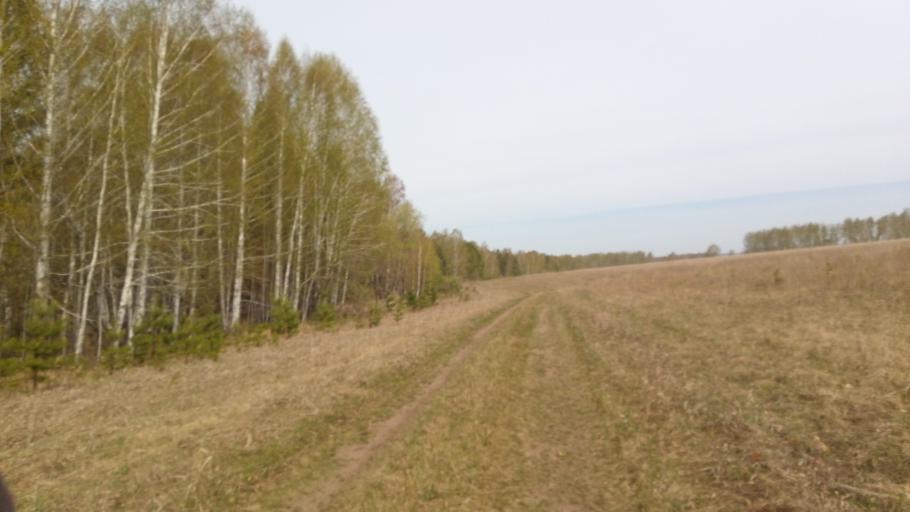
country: RU
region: Chelyabinsk
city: Timiryazevskiy
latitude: 55.0165
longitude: 60.8618
